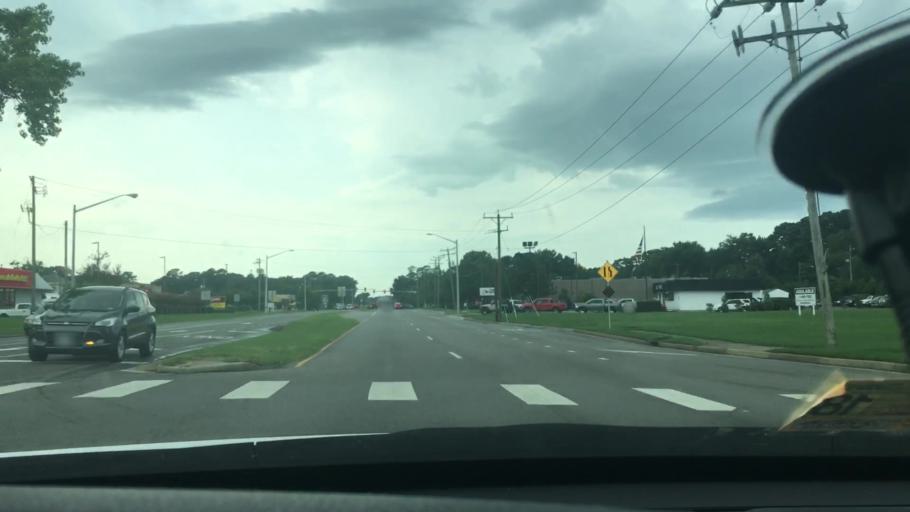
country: US
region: Virginia
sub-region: City of Virginia Beach
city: Virginia Beach
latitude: 36.9040
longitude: -76.1323
